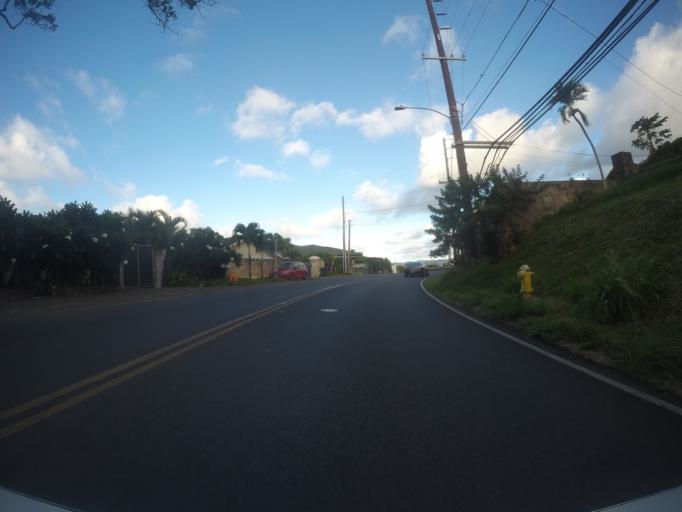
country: US
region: Hawaii
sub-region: Honolulu County
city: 'Ahuimanu
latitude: 21.4540
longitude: -157.8166
